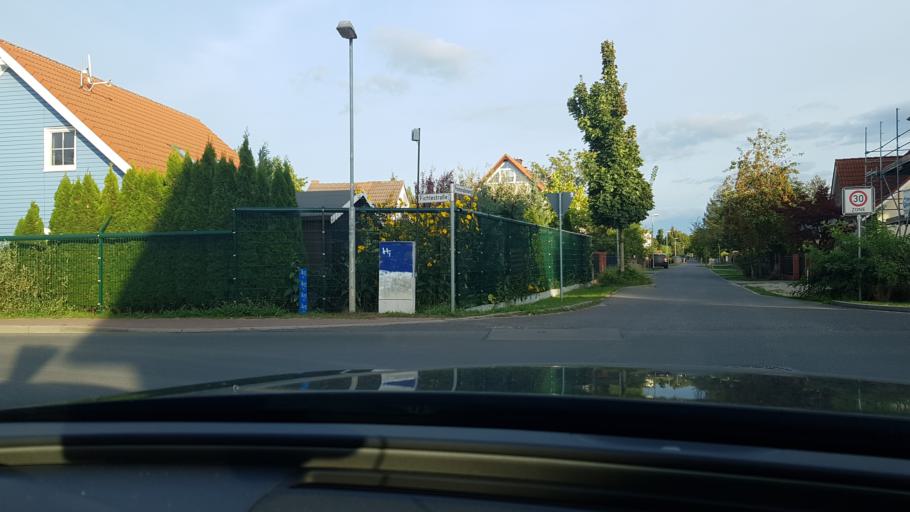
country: DE
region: Brandenburg
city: Brieselang
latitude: 52.5915
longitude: 12.9840
